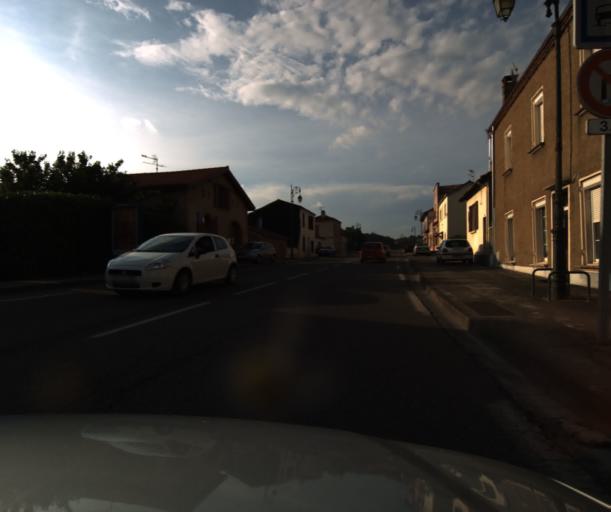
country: FR
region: Midi-Pyrenees
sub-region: Departement du Tarn-et-Garonne
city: Moissac
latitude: 44.0963
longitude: 1.0826
